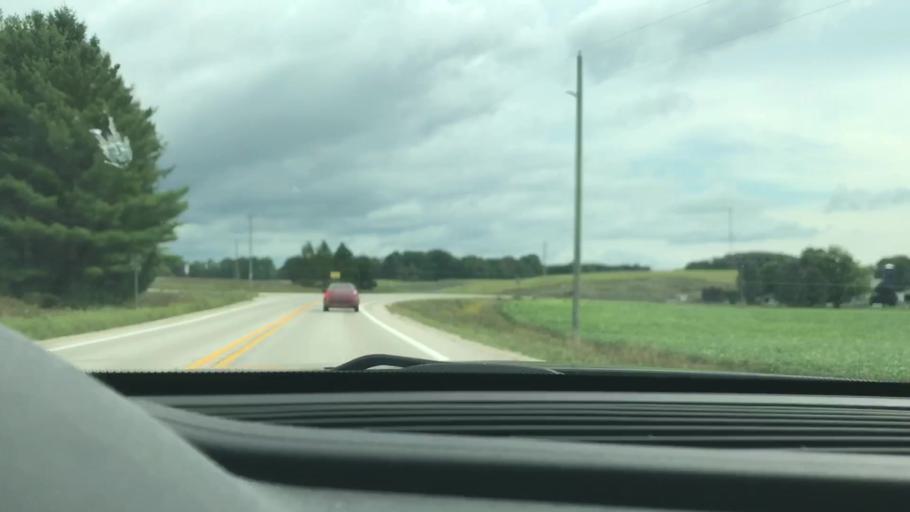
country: US
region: Michigan
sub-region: Antrim County
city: Bellaire
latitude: 45.0933
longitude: -85.2915
